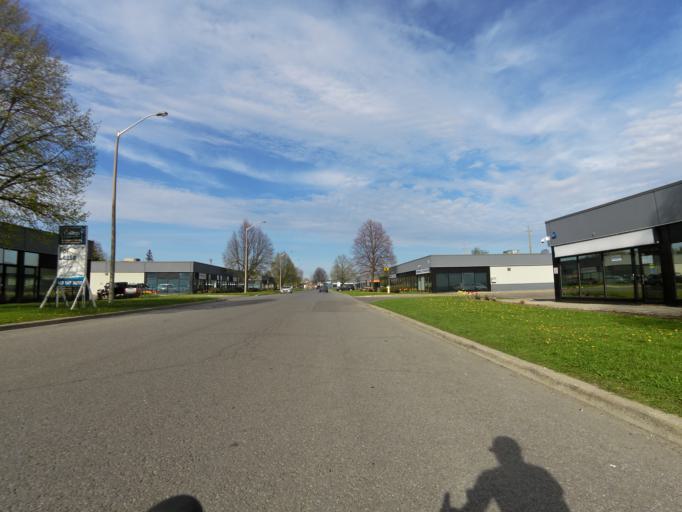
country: CA
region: Ontario
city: Ottawa
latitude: 45.3301
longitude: -75.7247
